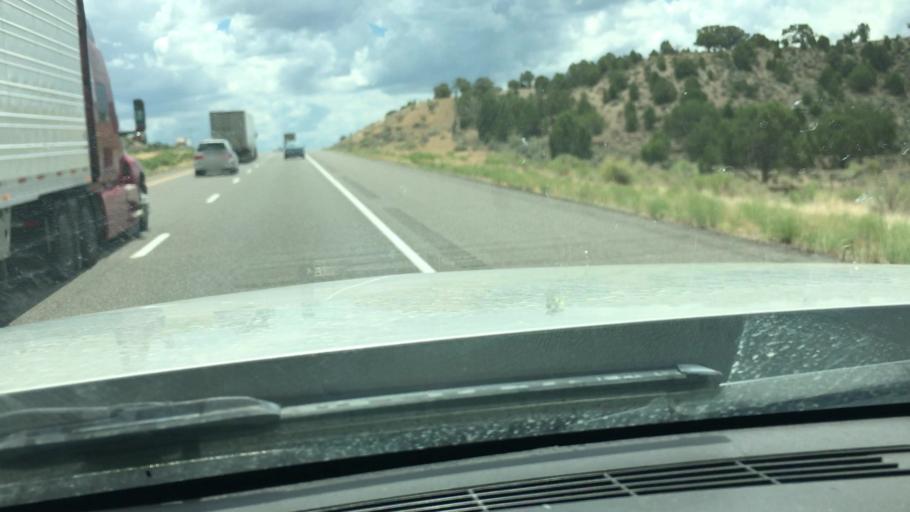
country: US
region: Utah
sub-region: Beaver County
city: Beaver
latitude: 38.3344
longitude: -112.6575
